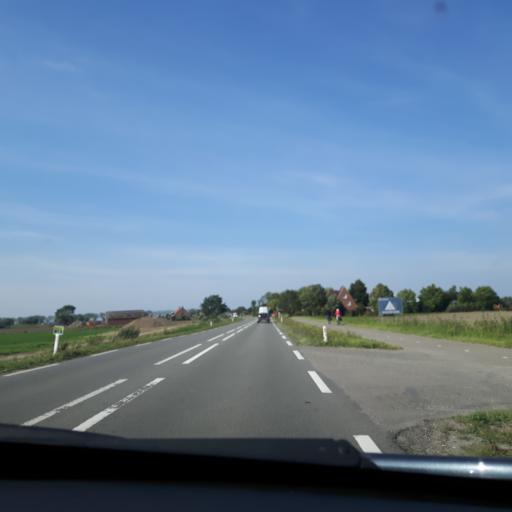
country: NL
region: Zeeland
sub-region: Gemeente Sluis
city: Sluis
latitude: 51.3328
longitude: 3.4708
